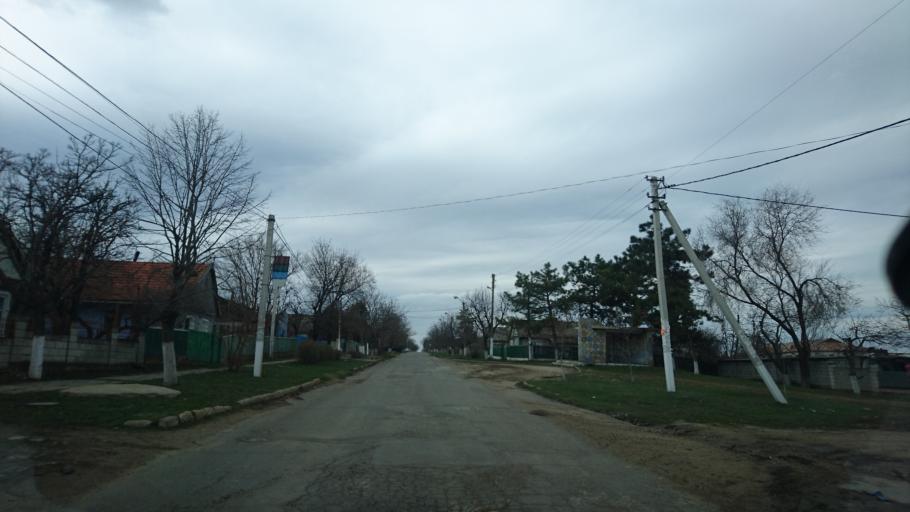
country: MD
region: Cantemir
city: Visniovca
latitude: 46.3334
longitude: 28.4458
